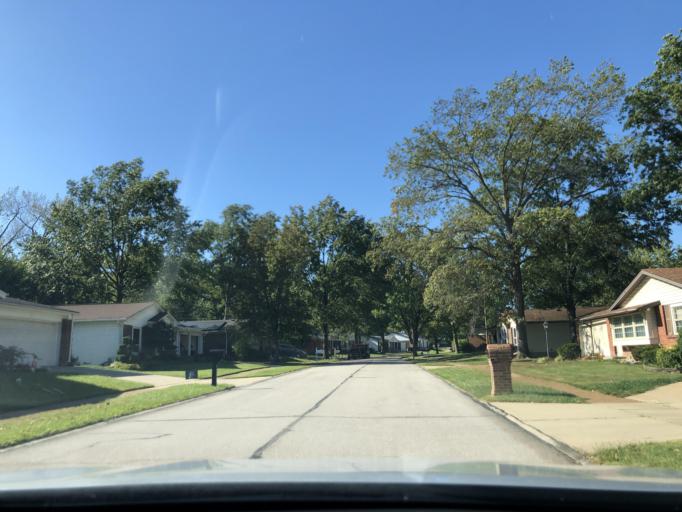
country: US
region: Missouri
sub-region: Saint Louis County
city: Concord
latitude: 38.4938
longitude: -90.3582
